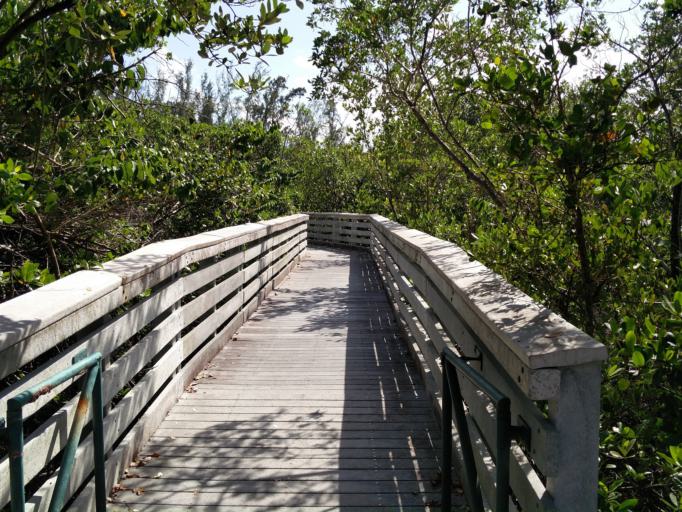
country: US
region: Florida
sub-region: Broward County
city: Dania Beach
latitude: 26.0379
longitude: -80.1194
